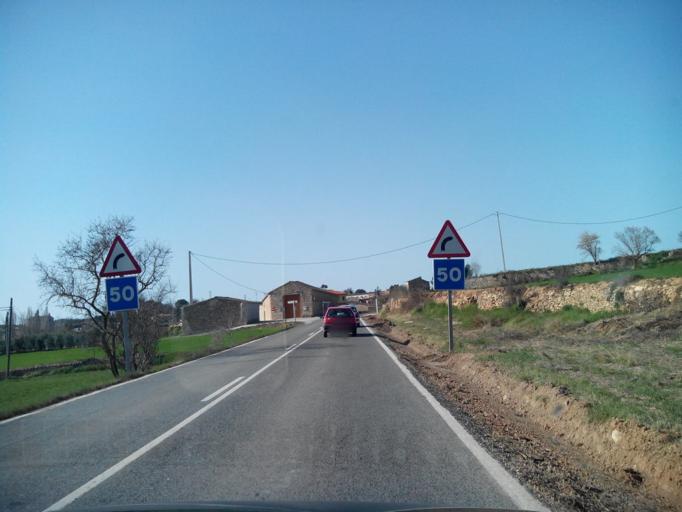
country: ES
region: Catalonia
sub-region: Provincia de Tarragona
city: Santa Coloma de Queralt
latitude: 41.5057
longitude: 1.3459
